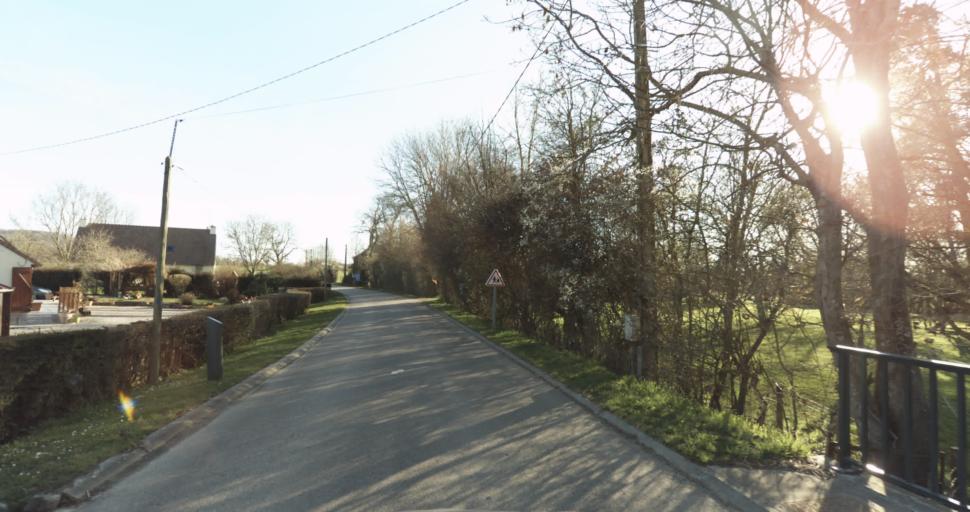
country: FR
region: Lower Normandy
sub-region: Departement du Calvados
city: Saint-Pierre-sur-Dives
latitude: 48.9623
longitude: 0.0512
